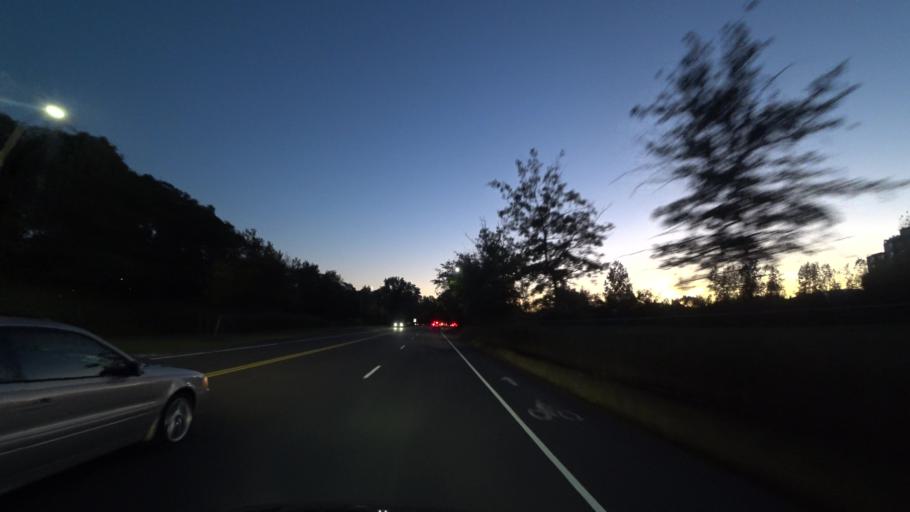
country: US
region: Massachusetts
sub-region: Middlesex County
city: Watertown
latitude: 42.3640
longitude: -71.1468
